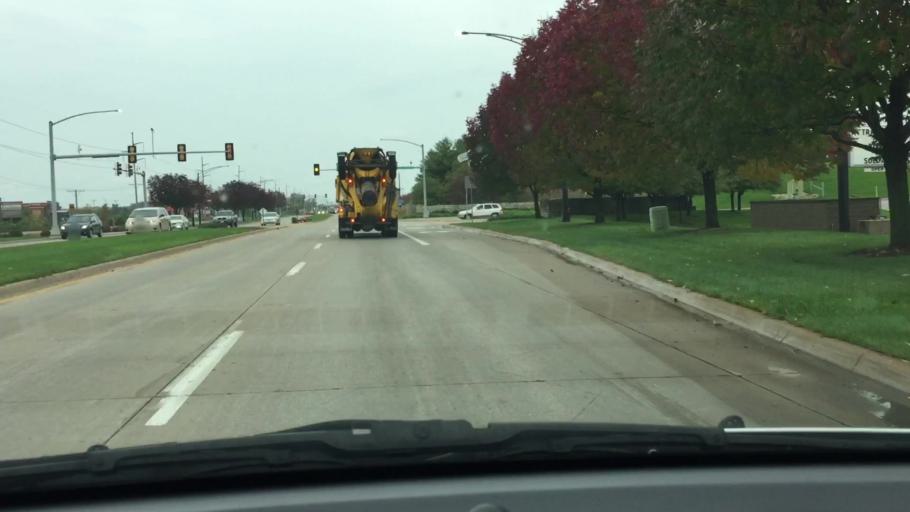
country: US
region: Iowa
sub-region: Johnson County
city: Coralville
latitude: 41.6868
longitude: -91.6055
